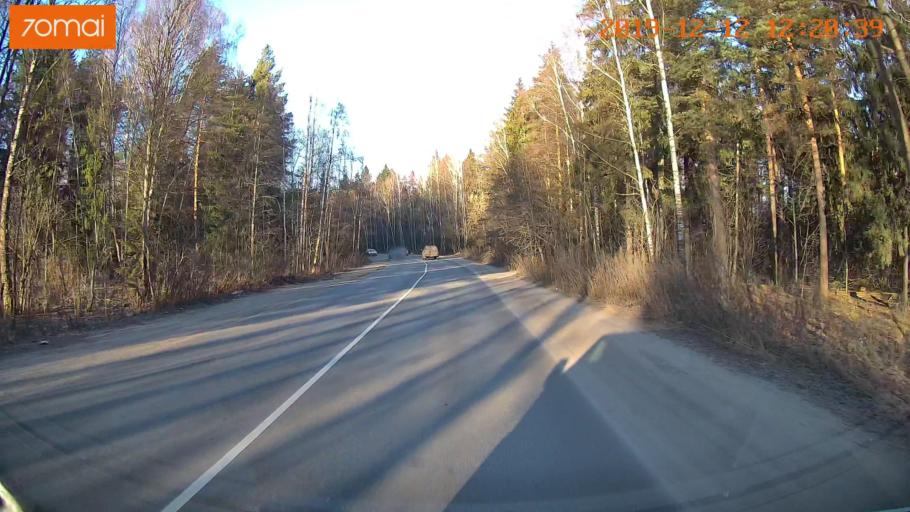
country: RU
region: Ivanovo
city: Kokhma
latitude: 56.9677
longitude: 41.0925
